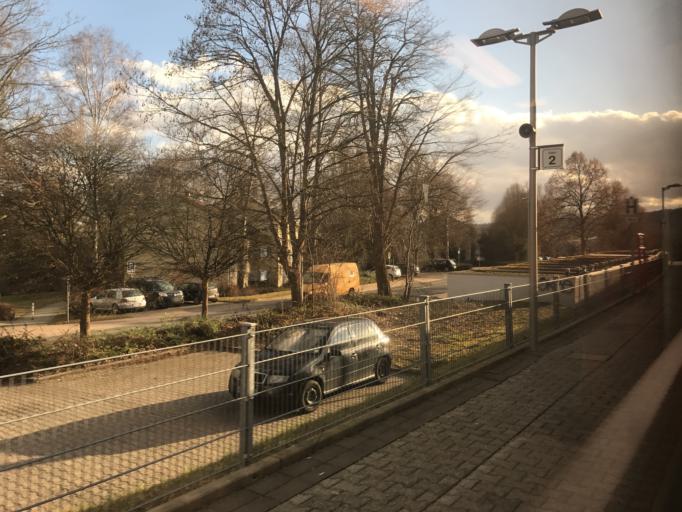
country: DE
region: Hesse
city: Kelkheim (Taunus)
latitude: 50.1469
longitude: 8.4445
